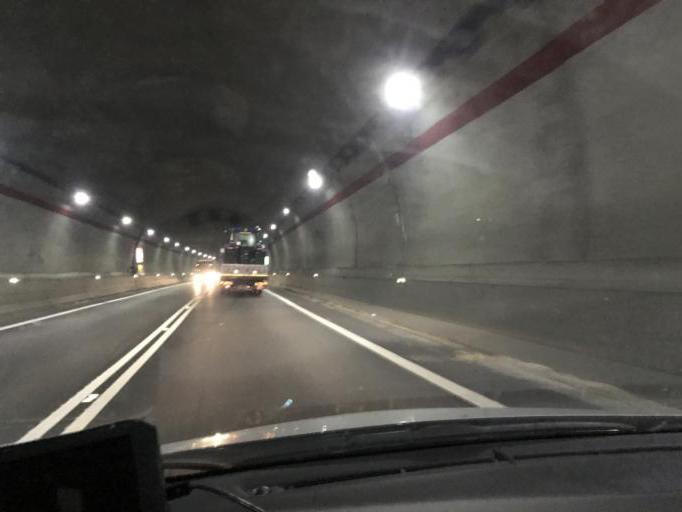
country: IT
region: Umbria
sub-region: Provincia di Terni
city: Terni
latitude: 42.5521
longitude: 12.7022
